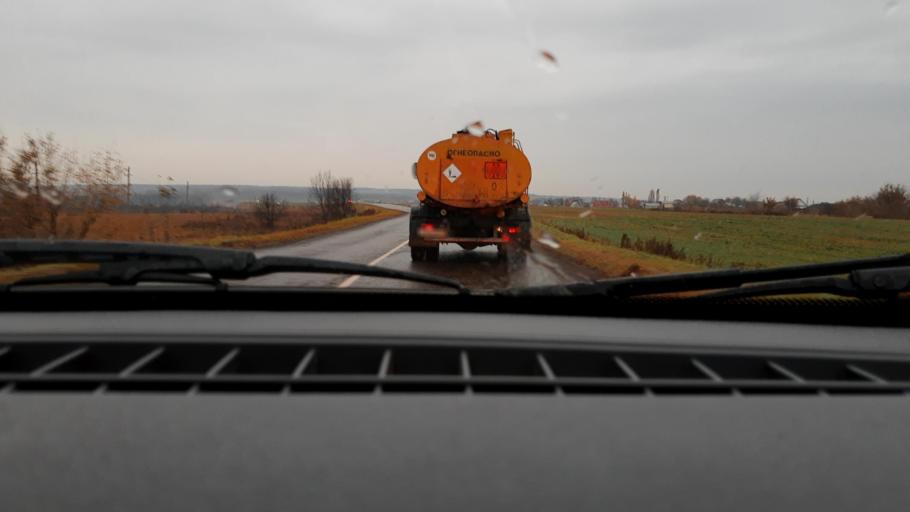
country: RU
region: Bashkortostan
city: Mikhaylovka
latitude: 54.8289
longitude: 55.9663
